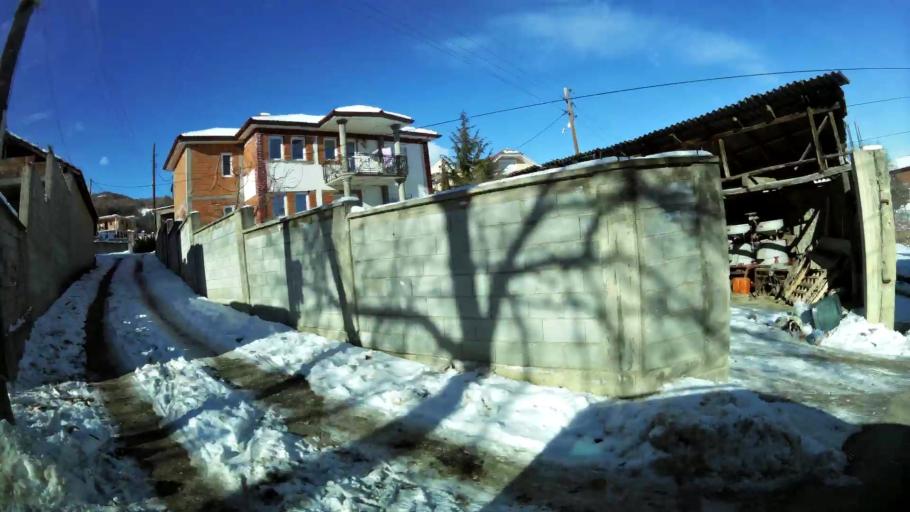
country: MK
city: Ljubin
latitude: 41.9784
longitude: 21.3020
